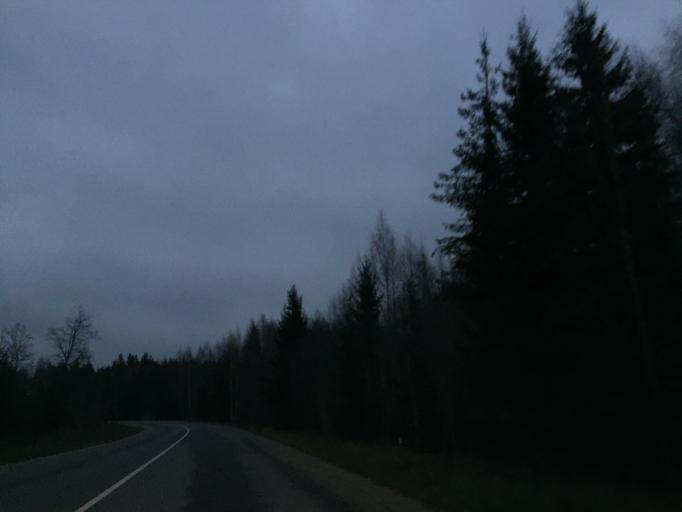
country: LV
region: Koceni
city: Koceni
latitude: 57.5483
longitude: 25.2707
